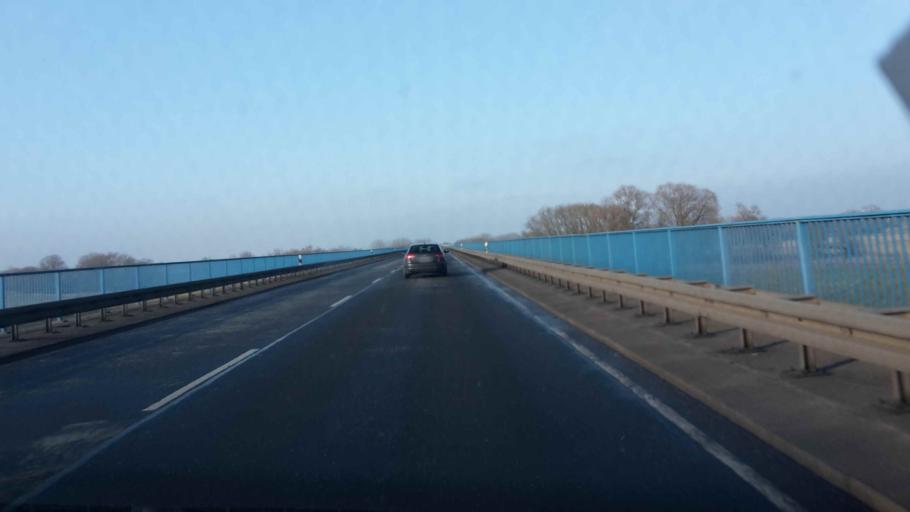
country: DE
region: Brandenburg
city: Wittenberge
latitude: 52.9803
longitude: 11.7313
